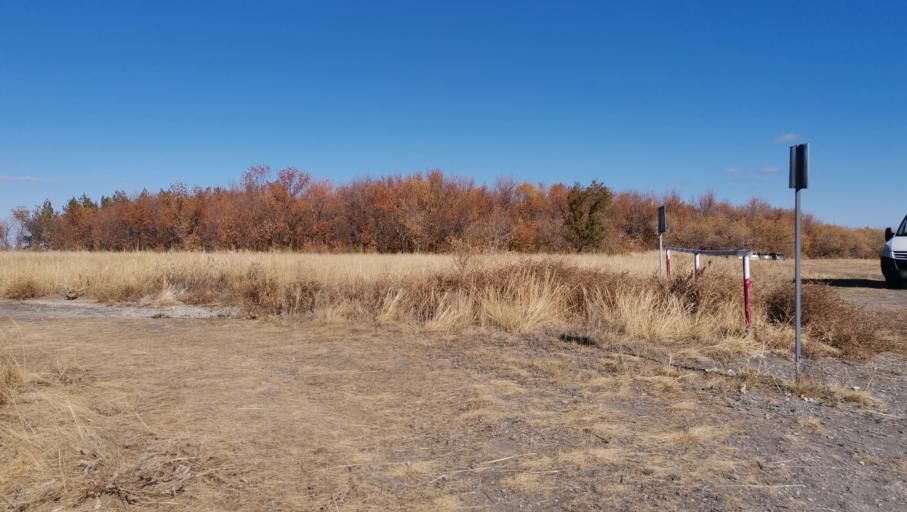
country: RU
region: Ulyanovsk
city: Novoul'yanovsk
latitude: 54.1124
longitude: 48.5763
